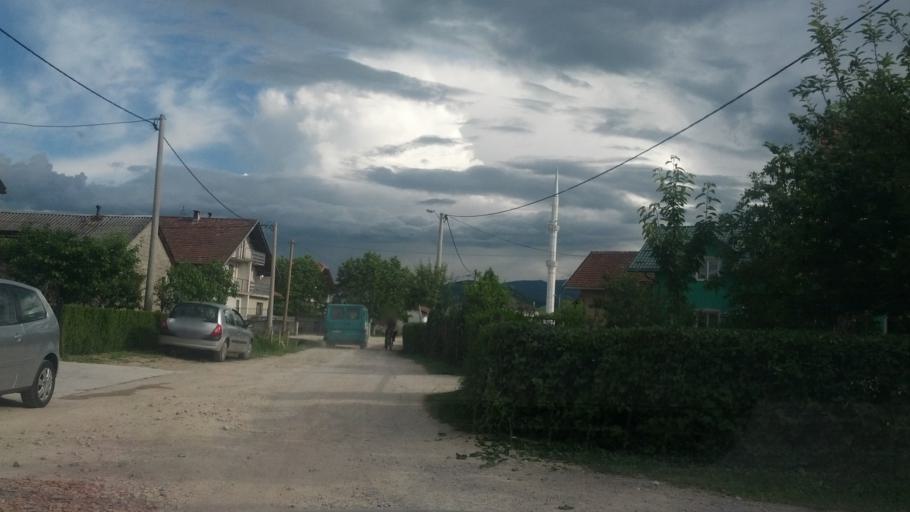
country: BA
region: Federation of Bosnia and Herzegovina
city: Bihac
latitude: 44.8384
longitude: 15.8759
